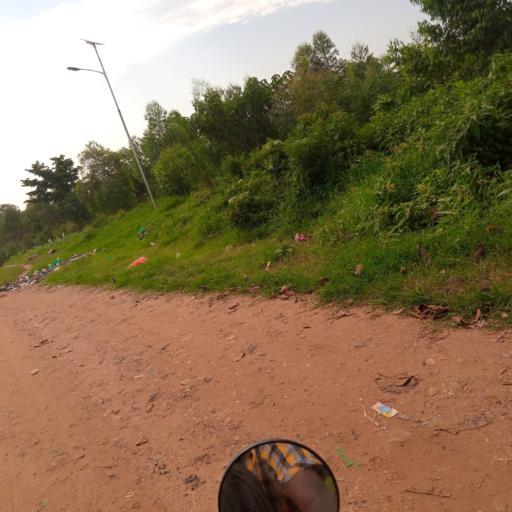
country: UG
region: Eastern Region
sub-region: Mbale District
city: Mbale
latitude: 1.0772
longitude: 34.1827
